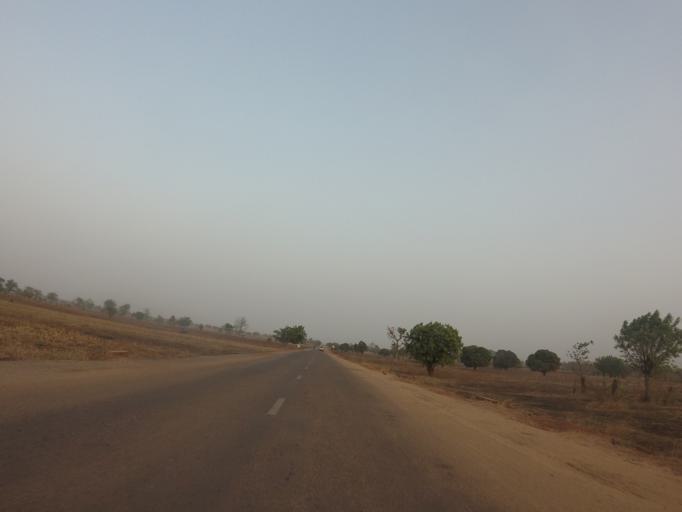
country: GH
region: Northern
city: Tamale
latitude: 9.4419
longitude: -1.1057
